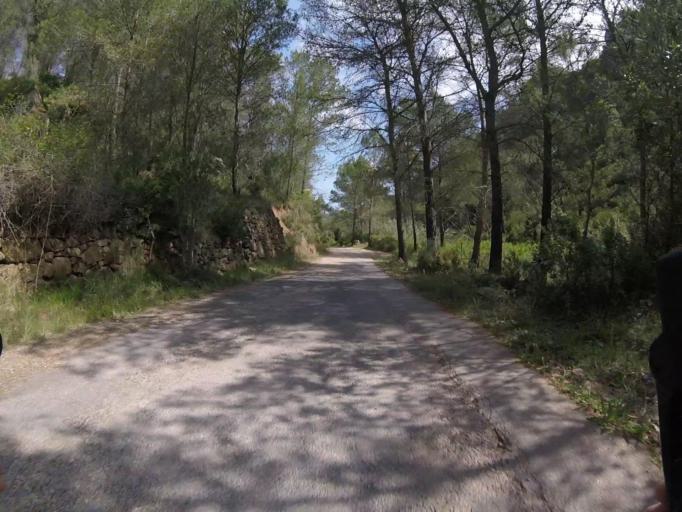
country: ES
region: Valencia
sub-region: Provincia de Castello
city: Cabanes
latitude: 40.1068
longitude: 0.0402
